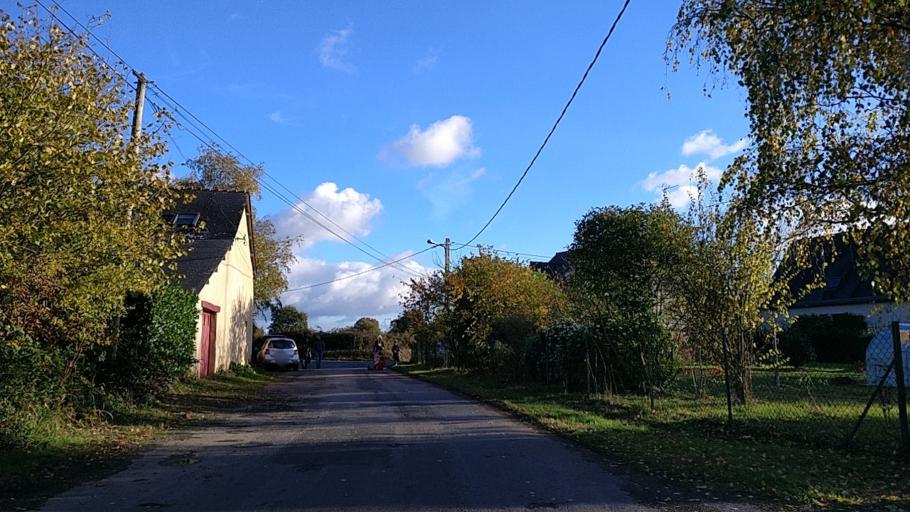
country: FR
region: Brittany
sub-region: Departement d'Ille-et-Vilaine
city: Fouillard
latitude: 48.1333
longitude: -1.5675
